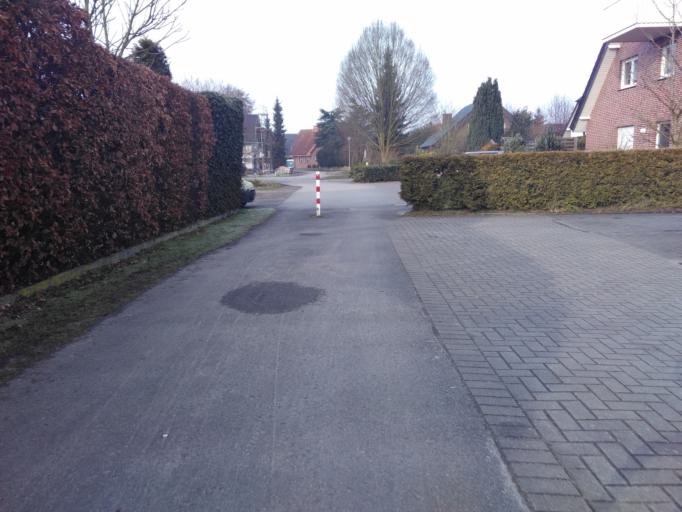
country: DE
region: North Rhine-Westphalia
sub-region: Regierungsbezirk Detmold
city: Verl
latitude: 51.8849
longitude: 8.4966
